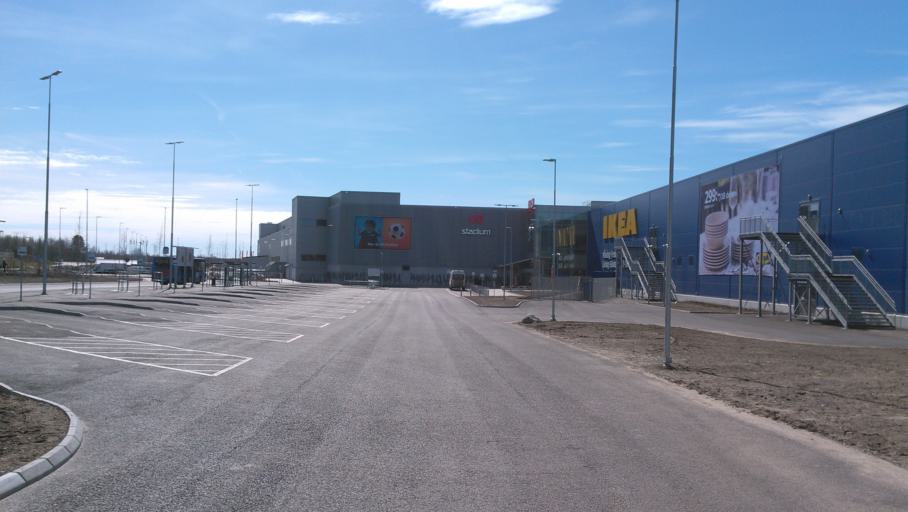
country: SE
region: Vaesterbotten
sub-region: Umea Kommun
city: Umea
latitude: 63.8086
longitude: 20.2576
